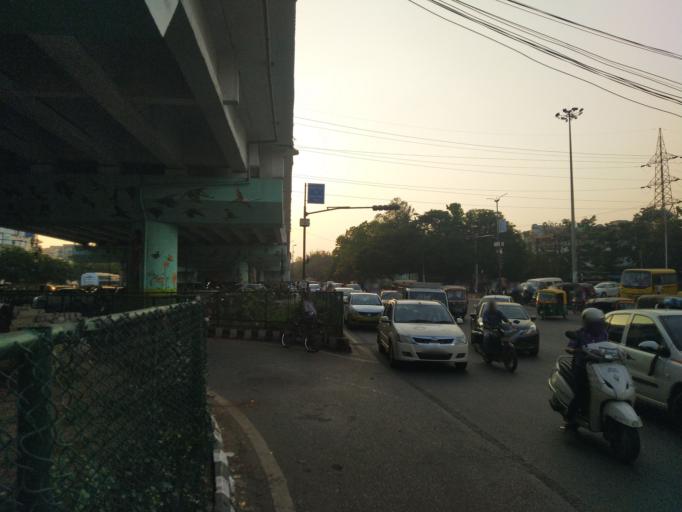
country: IN
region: Odisha
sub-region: Khordha
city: Bhubaneshwar
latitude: 20.2972
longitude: 85.8337
